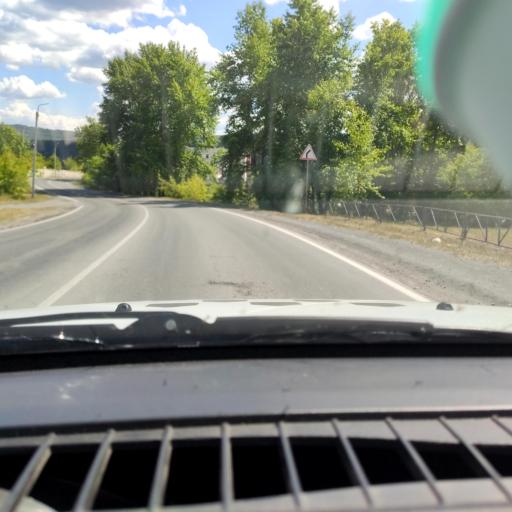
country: RU
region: Chelyabinsk
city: Satka
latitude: 55.0369
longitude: 58.9820
